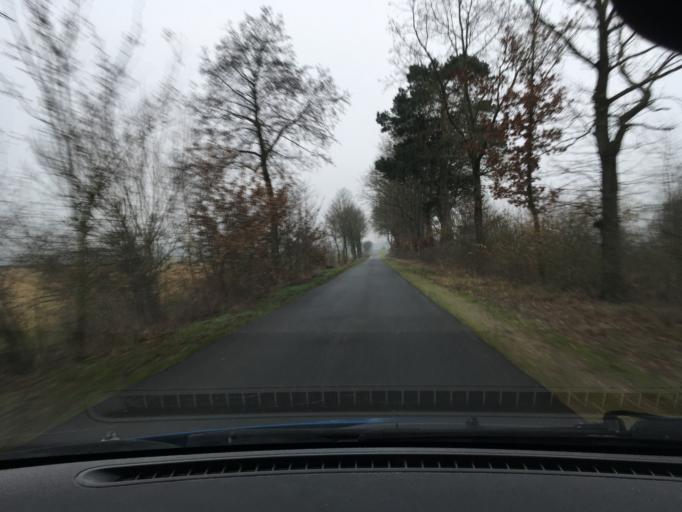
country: DE
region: Lower Saxony
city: Soderstorf
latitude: 53.0977
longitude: 10.1637
